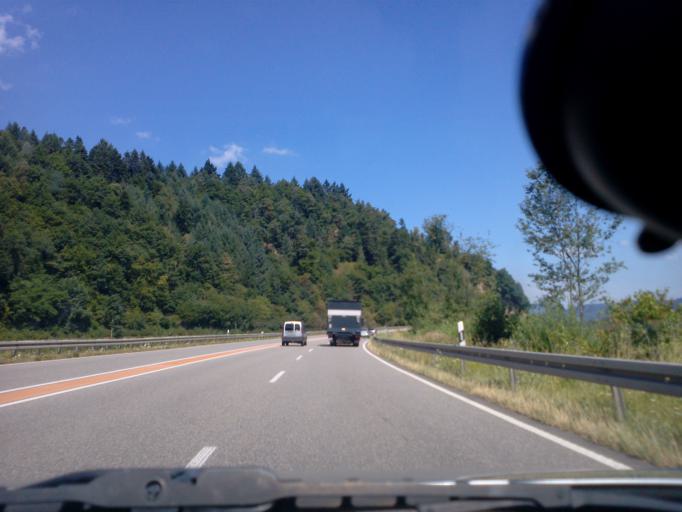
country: DE
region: Baden-Wuerttemberg
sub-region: Freiburg Region
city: Biberach
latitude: 48.3368
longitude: 8.0204
